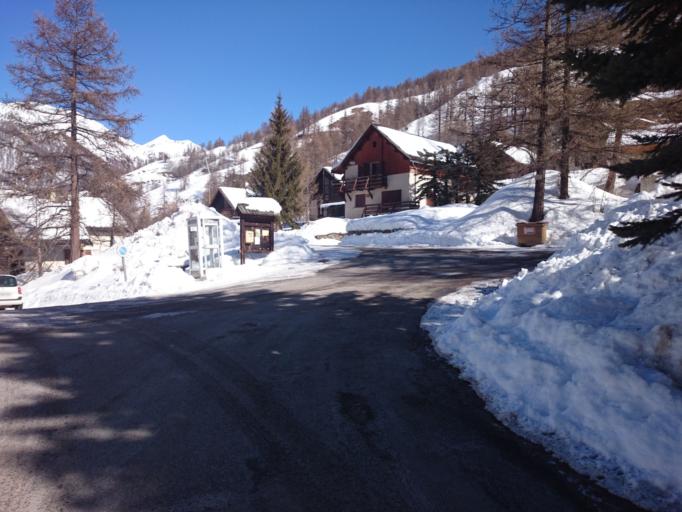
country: IT
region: Piedmont
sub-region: Provincia di Torino
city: Prali
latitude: 44.7876
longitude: 6.9329
